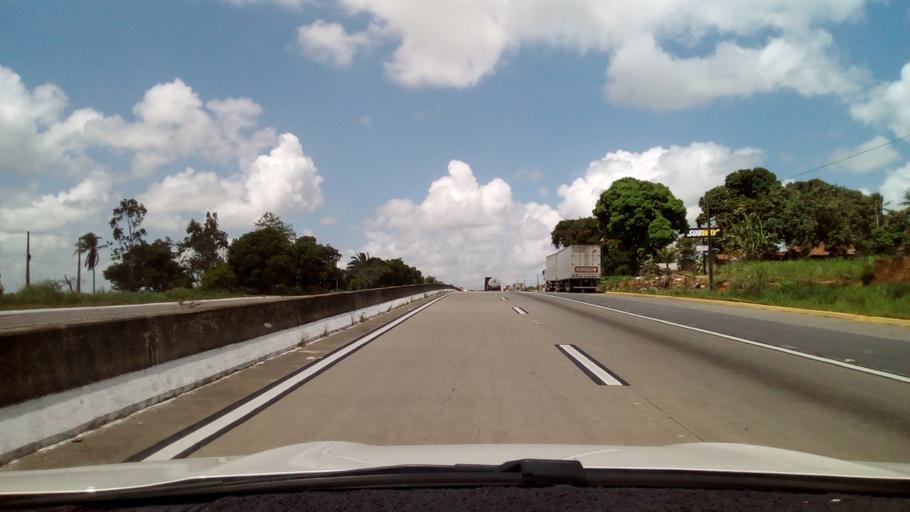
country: BR
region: Paraiba
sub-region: Alhandra
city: Alhandra
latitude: -7.3657
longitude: -34.9529
